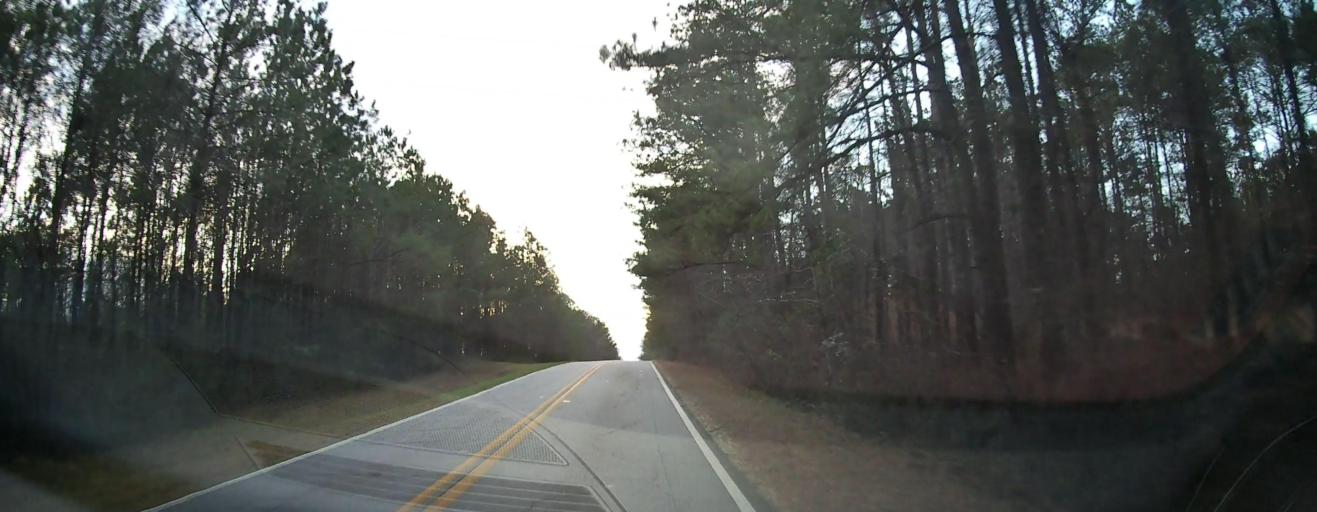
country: US
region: Alabama
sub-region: Russell County
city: Phenix City
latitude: 32.5970
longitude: -84.9000
